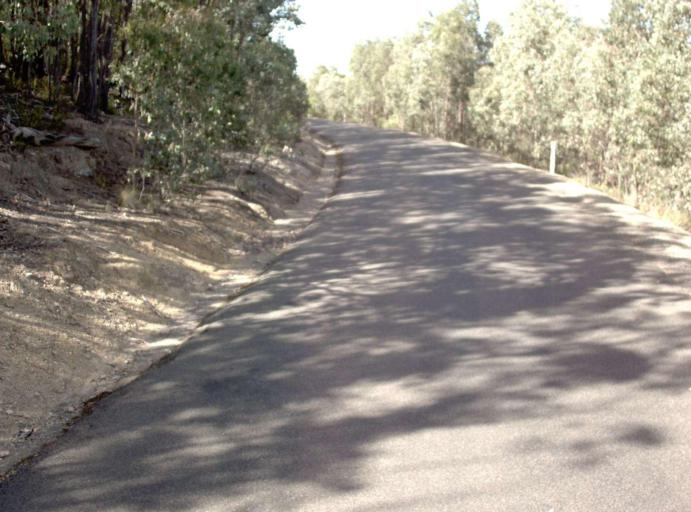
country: AU
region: Victoria
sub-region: East Gippsland
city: Lakes Entrance
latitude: -37.4757
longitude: 148.1248
